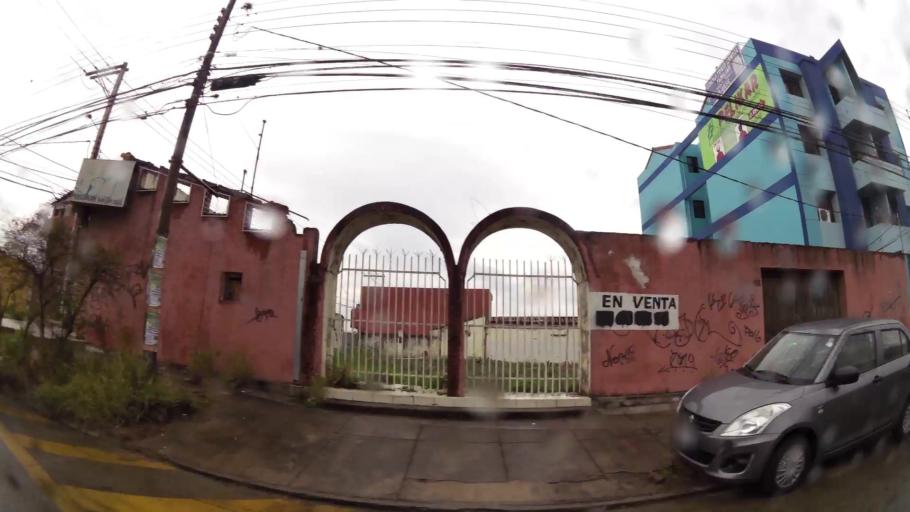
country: BO
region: Santa Cruz
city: Santa Cruz de la Sierra
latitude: -17.7723
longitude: -63.1593
